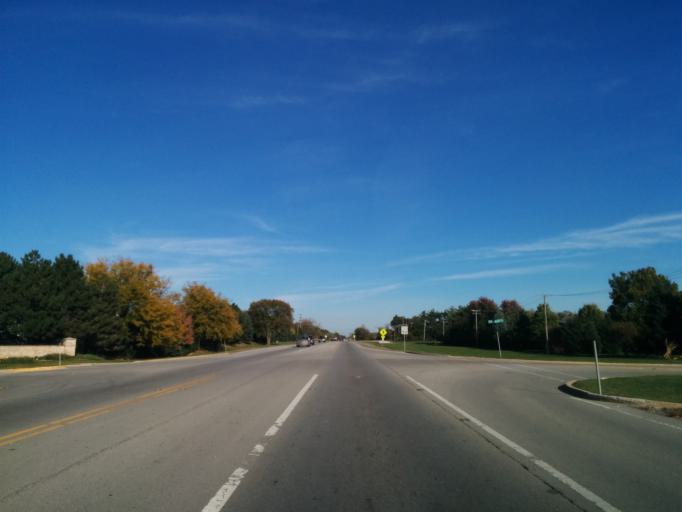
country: US
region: Illinois
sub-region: Kane County
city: Batavia
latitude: 41.8146
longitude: -88.2694
